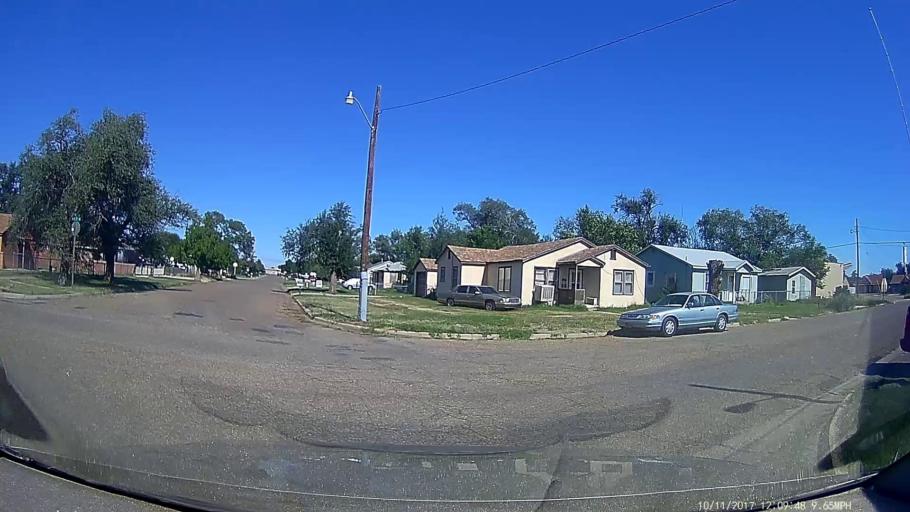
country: US
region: New Mexico
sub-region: Curry County
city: Clovis
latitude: 34.4116
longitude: -103.2149
